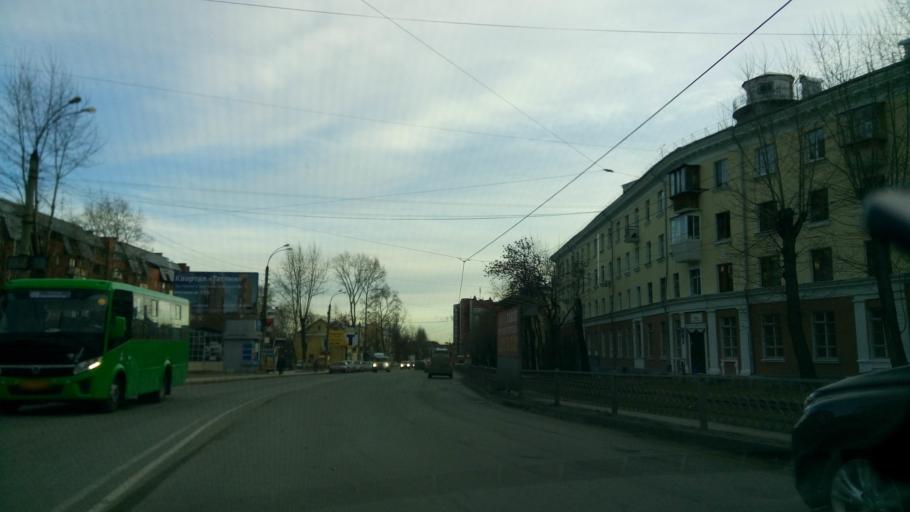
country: RU
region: Sverdlovsk
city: Shuvakish
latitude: 56.8739
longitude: 60.5182
